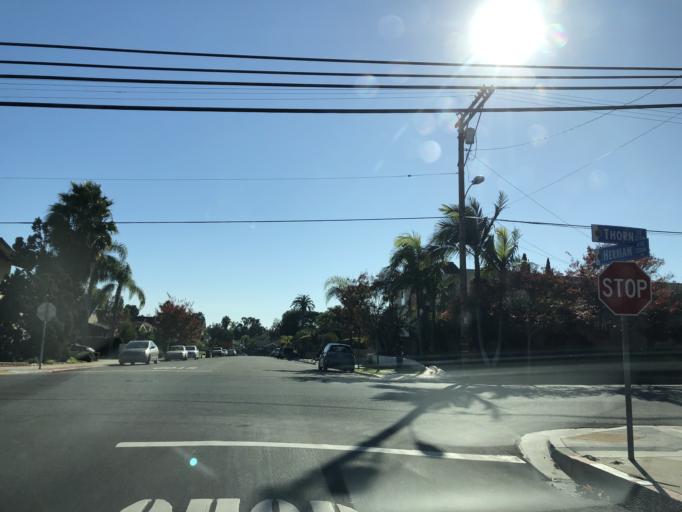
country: US
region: California
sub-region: San Diego County
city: San Diego
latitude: 32.7394
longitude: -117.1261
